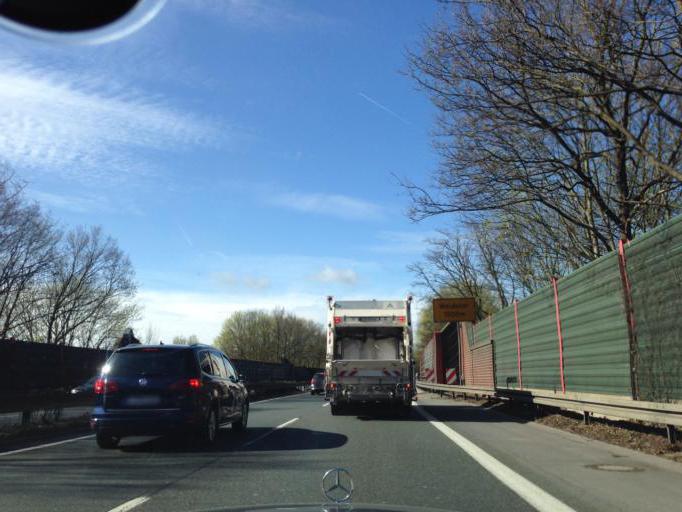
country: DE
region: Lower Saxony
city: Isernhagen Farster Bauerschaft
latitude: 52.4010
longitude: 9.8135
